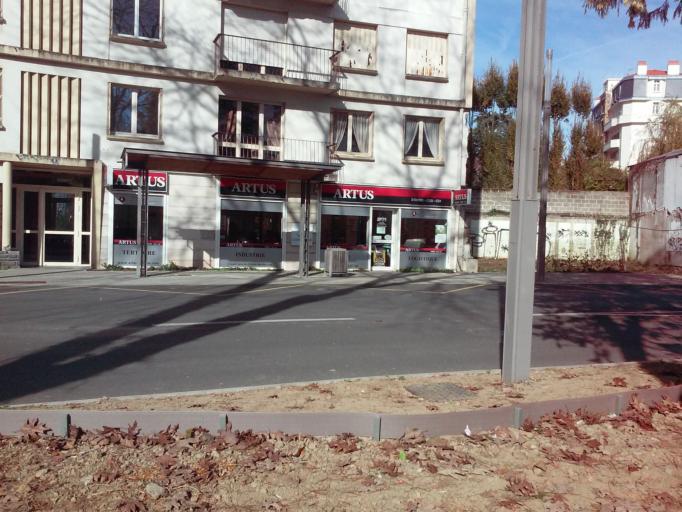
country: FR
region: Pays de la Loire
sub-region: Departement de la Vendee
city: La Roche-sur-Yon
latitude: 46.6697
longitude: -1.4324
